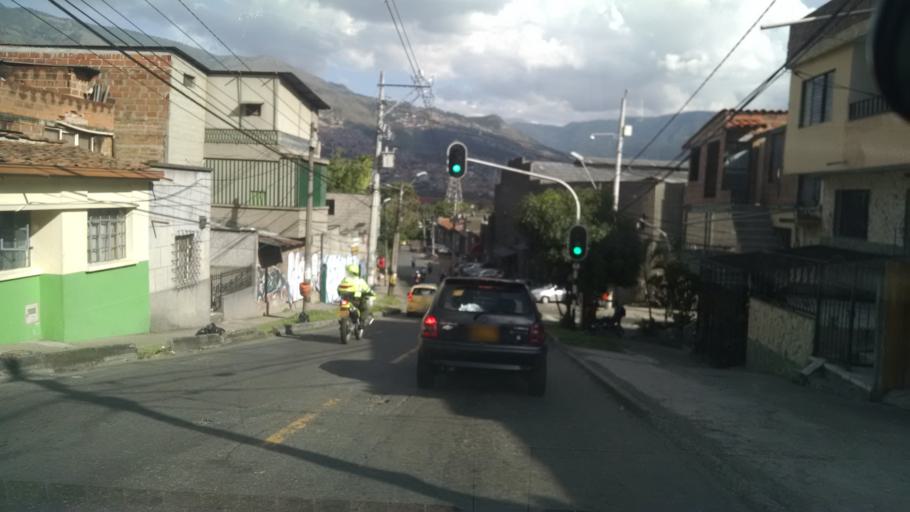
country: CO
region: Antioquia
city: Medellin
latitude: 6.2776
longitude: -75.5756
